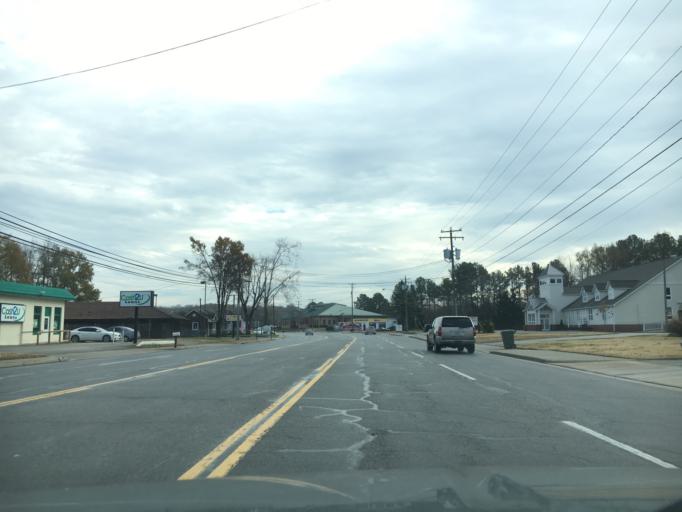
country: US
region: Virginia
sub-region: Prince Edward County
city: Farmville
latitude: 37.3061
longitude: -78.4151
